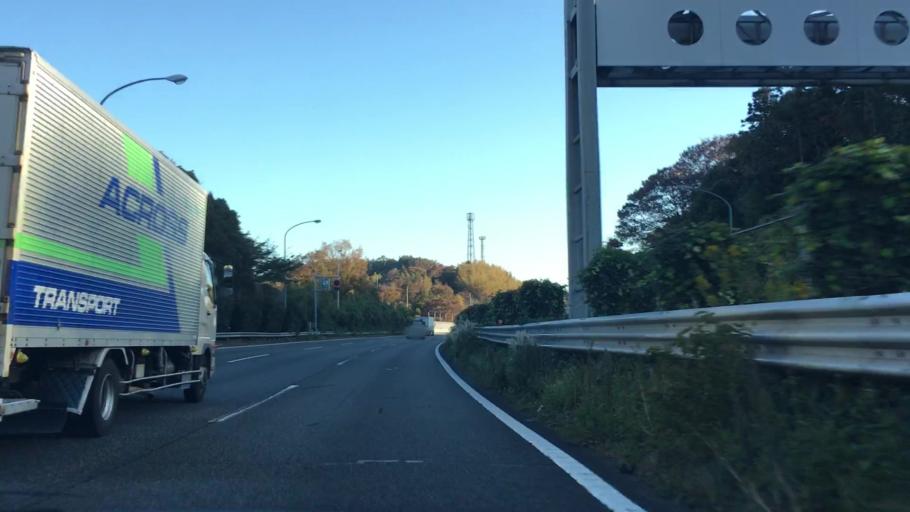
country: JP
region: Tokyo
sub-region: Machida-shi
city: Machida
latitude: 35.5122
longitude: 139.4875
